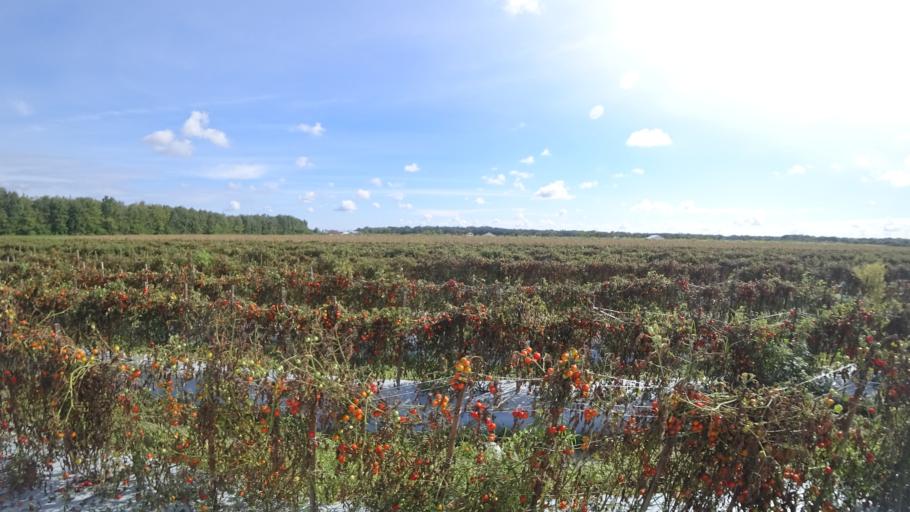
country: US
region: Florida
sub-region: Sarasota County
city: The Meadows
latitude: 27.4464
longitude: -82.3120
